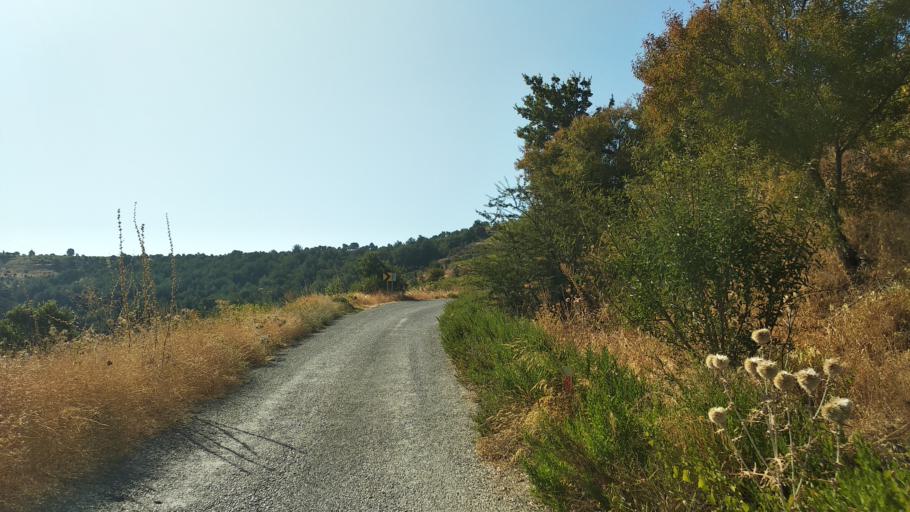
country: TR
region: Izmir
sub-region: Seferihisar
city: Seferhisar
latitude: 38.3288
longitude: 26.9490
